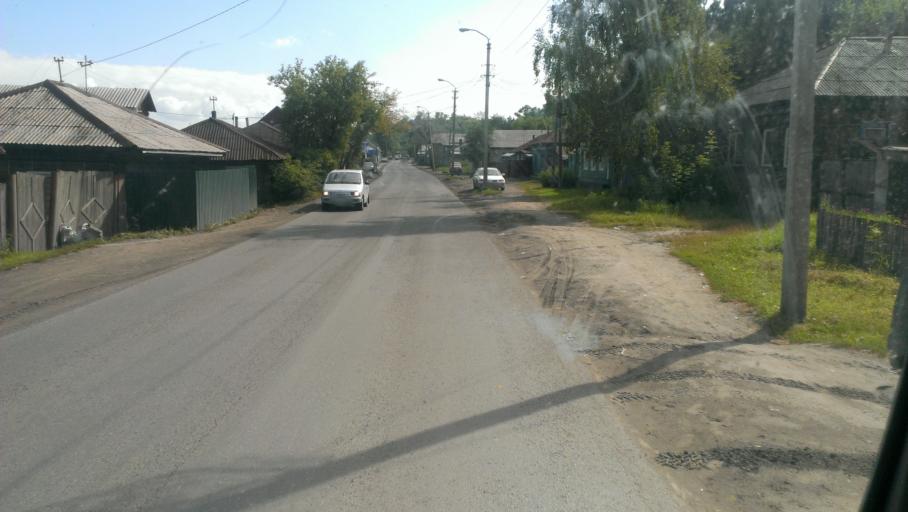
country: RU
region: Altai Krai
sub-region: Gorod Barnaulskiy
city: Barnaul
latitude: 53.3192
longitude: 83.7717
